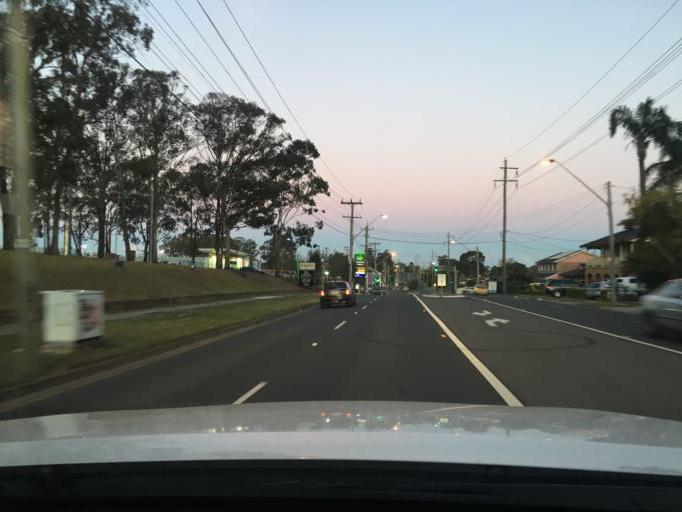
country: AU
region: New South Wales
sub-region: Holroyd
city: Girraween
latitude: -33.8298
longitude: 150.9502
